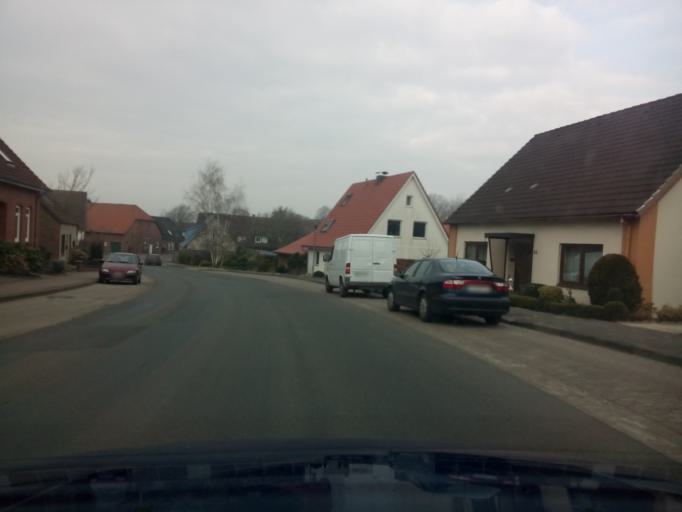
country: DE
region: Lower Saxony
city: Lintig
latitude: 53.6191
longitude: 8.8468
